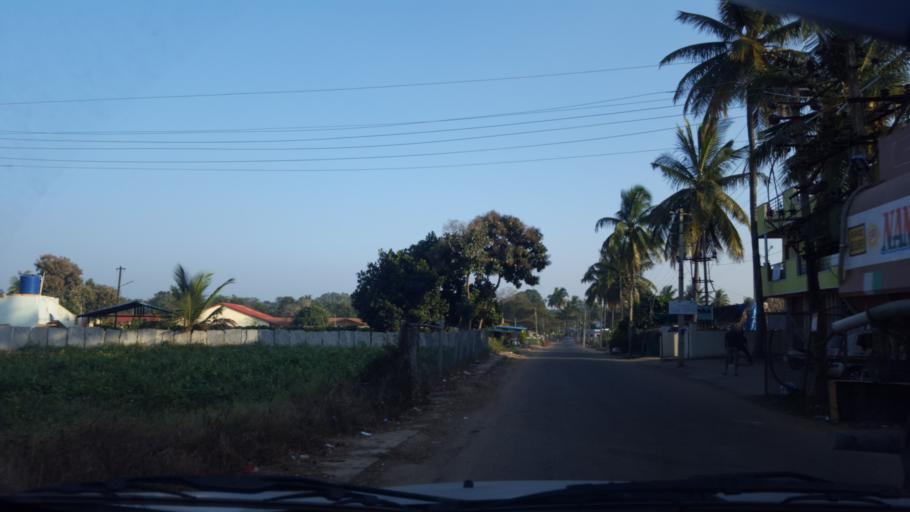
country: IN
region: Karnataka
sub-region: Bangalore Urban
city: Yelahanka
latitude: 13.1784
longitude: 77.5889
